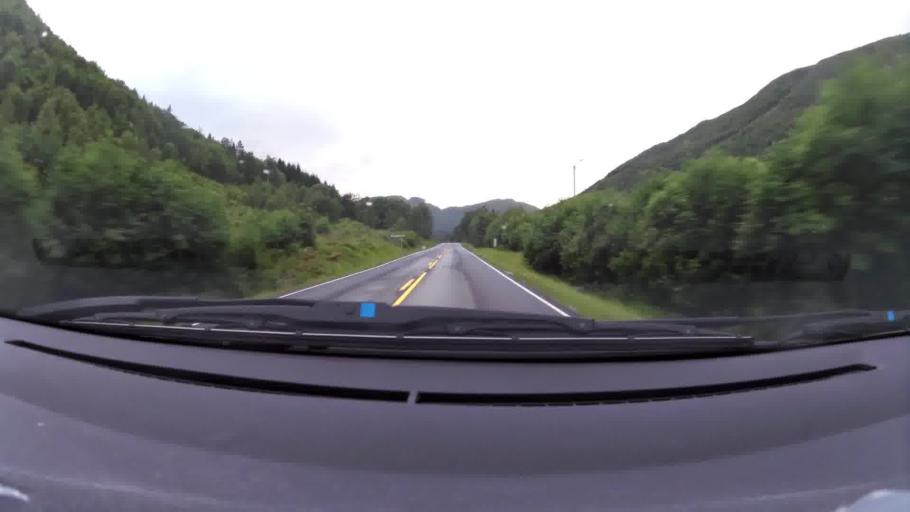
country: NO
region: More og Romsdal
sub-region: Molde
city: Molde
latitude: 62.7962
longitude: 7.2828
